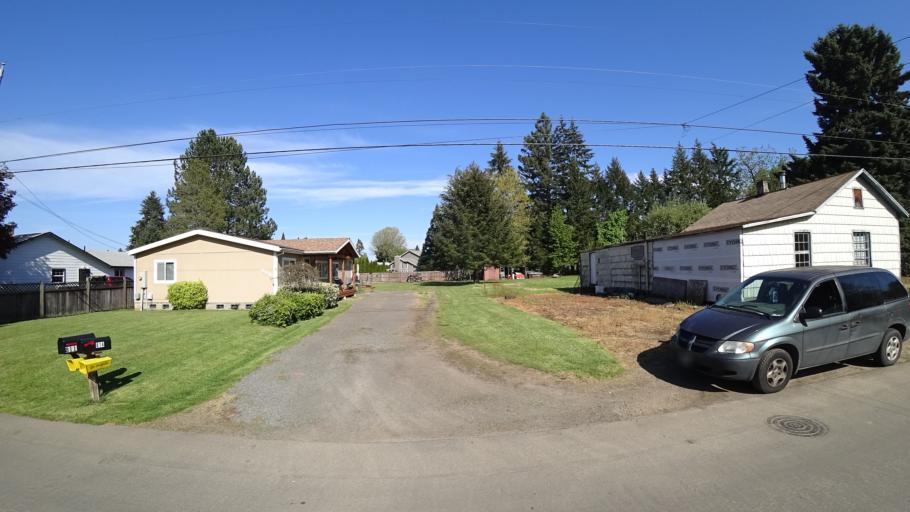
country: US
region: Oregon
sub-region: Washington County
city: Hillsboro
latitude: 45.5303
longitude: -122.9844
